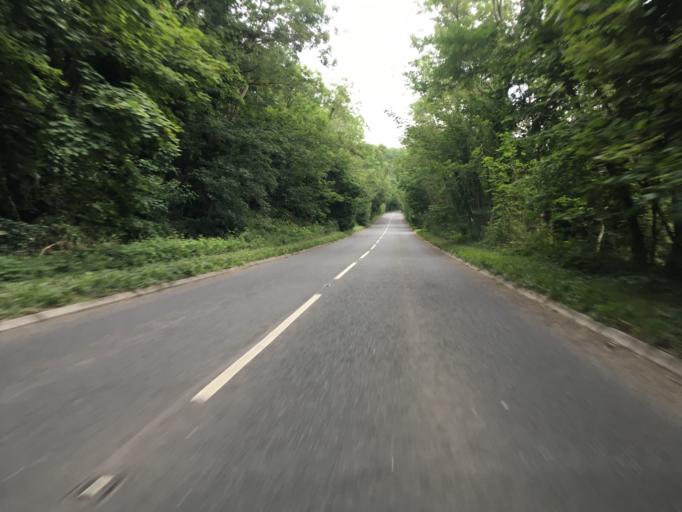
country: GB
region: England
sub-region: North Somerset
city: Long Ashton
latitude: 51.4310
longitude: -2.6955
